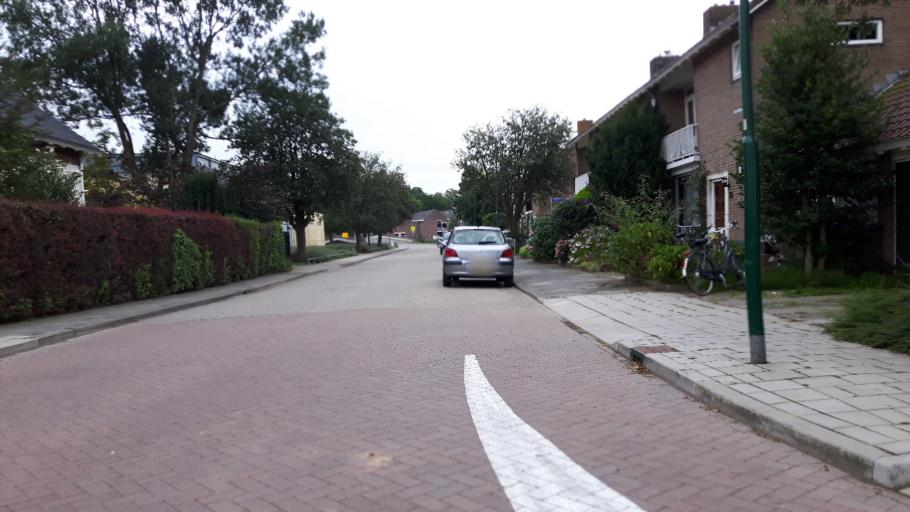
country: NL
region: Utrecht
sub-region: Gemeente Woerden
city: Woerden
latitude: 52.0914
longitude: 4.8859
